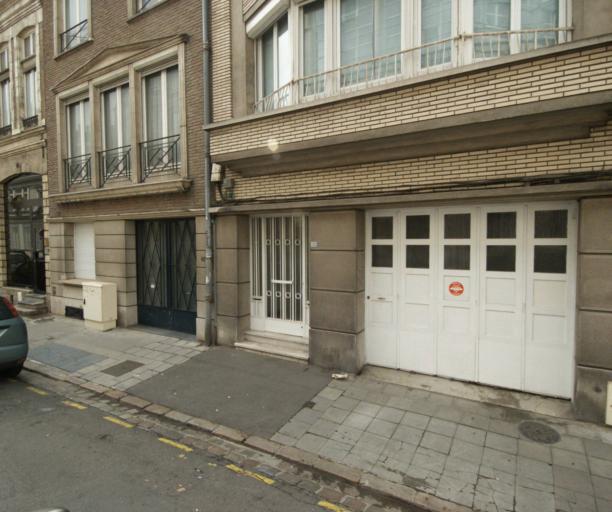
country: FR
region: Nord-Pas-de-Calais
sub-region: Departement du Nord
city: Lille
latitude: 50.6366
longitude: 3.0588
